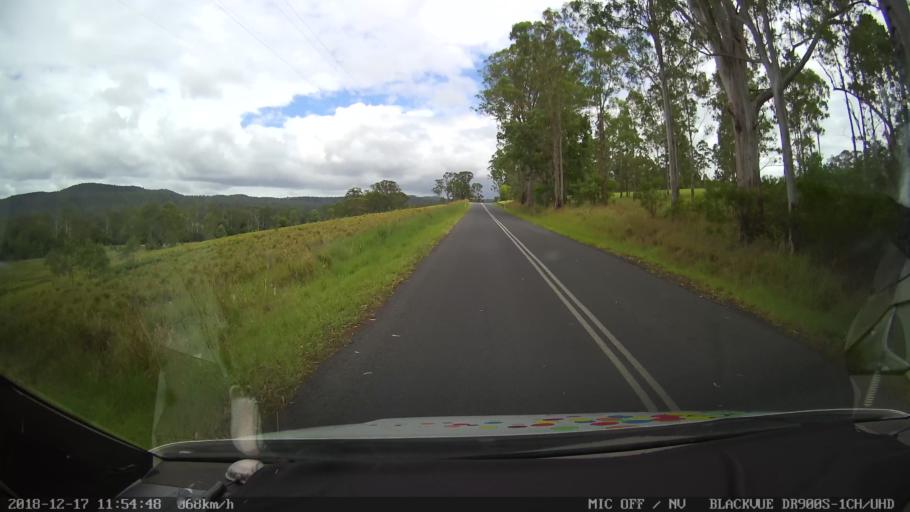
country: AU
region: New South Wales
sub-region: Kyogle
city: Kyogle
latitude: -28.5625
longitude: 152.5817
